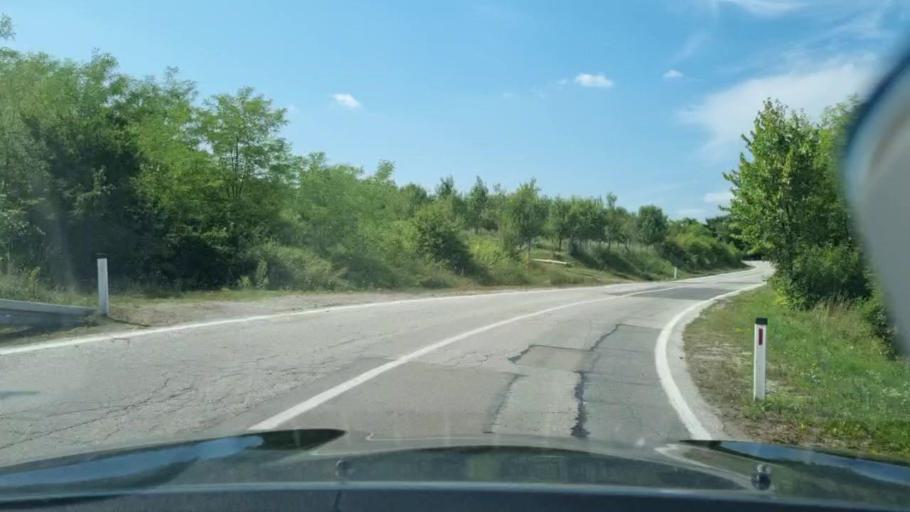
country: BA
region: Federation of Bosnia and Herzegovina
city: Bosanska Krupa
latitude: 44.8310
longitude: 16.1679
